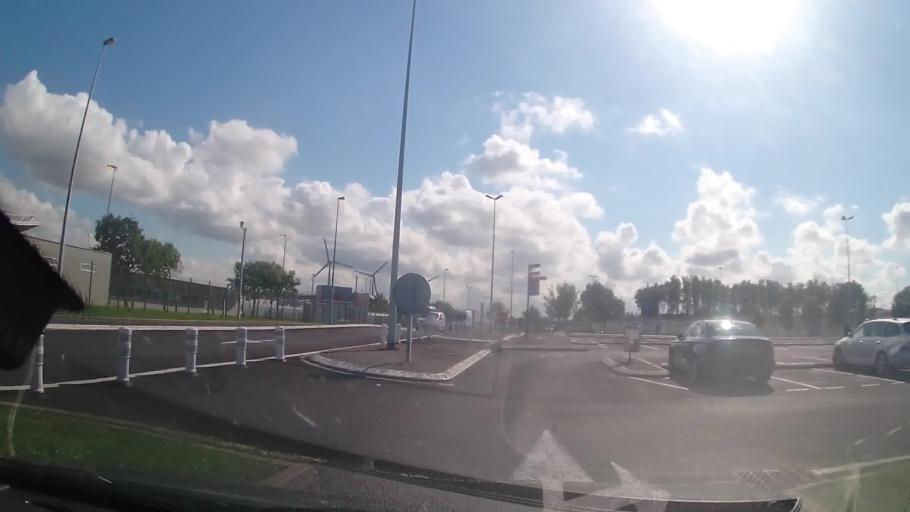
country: FR
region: Nord-Pas-de-Calais
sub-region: Departement du Pas-de-Calais
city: Coquelles
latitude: 50.9347
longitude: 1.8132
